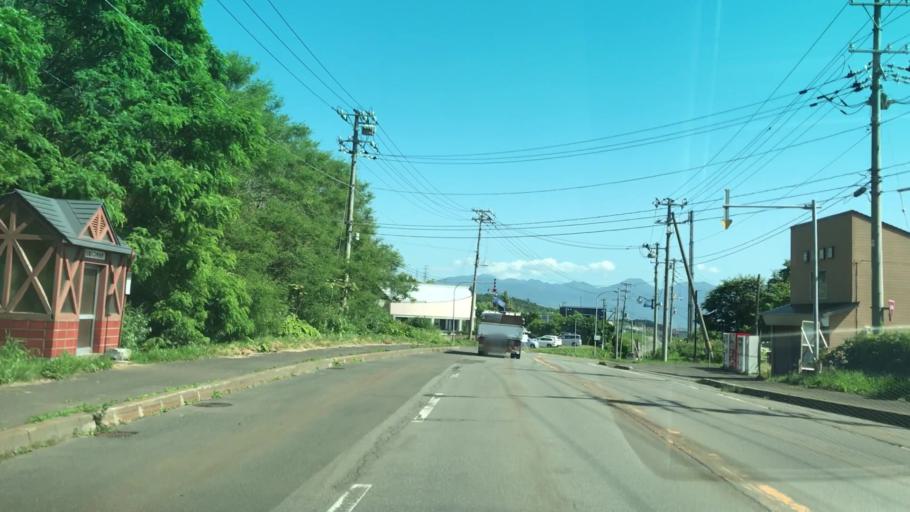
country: JP
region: Hokkaido
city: Iwanai
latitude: 43.0592
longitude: 140.4978
